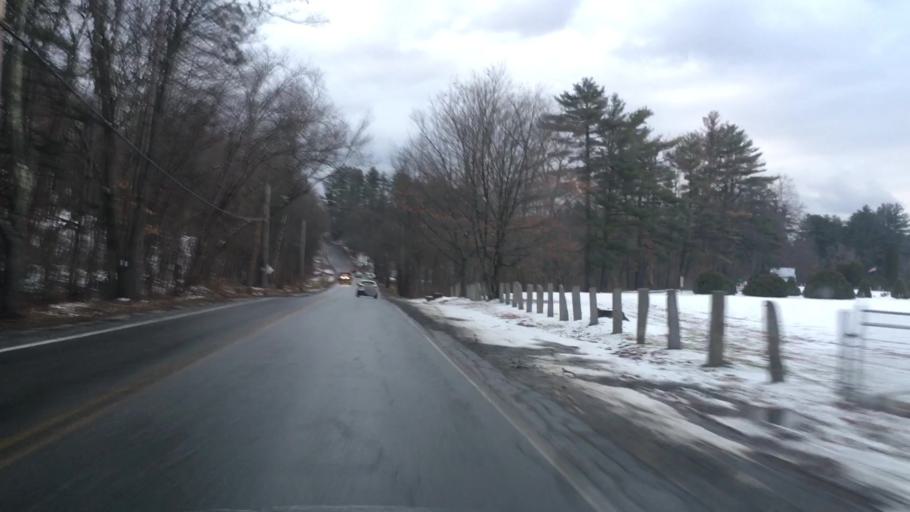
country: US
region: New Hampshire
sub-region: Sullivan County
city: Claremont
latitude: 43.3849
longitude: -72.3502
